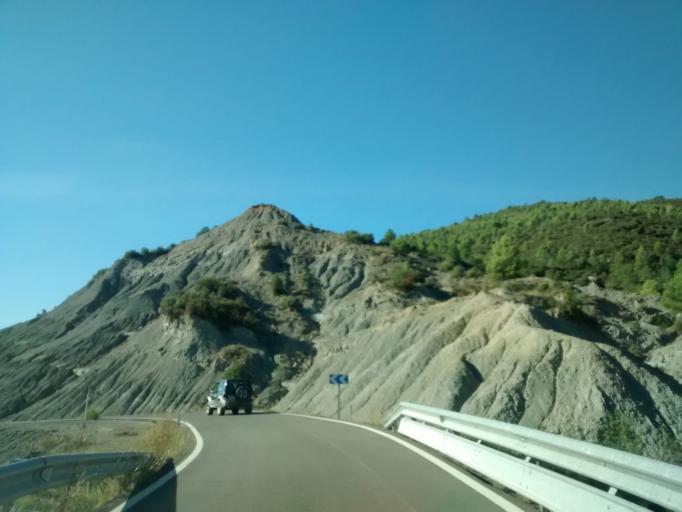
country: ES
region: Aragon
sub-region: Provincia de Huesca
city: Loarre
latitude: 42.3867
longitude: -0.7012
